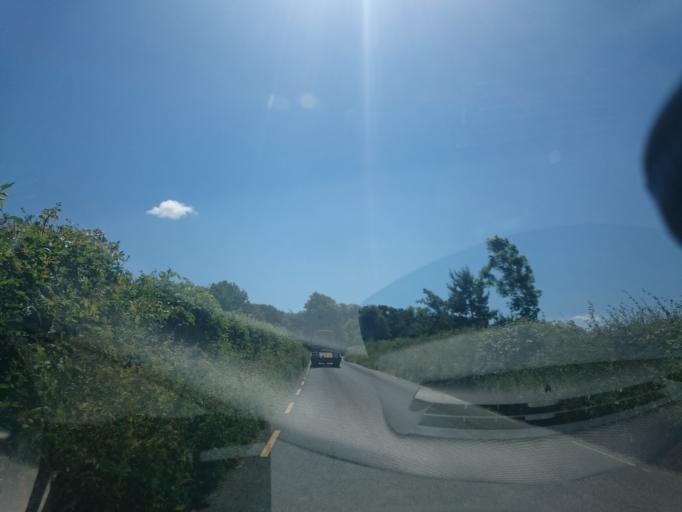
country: IE
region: Leinster
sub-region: Kilkenny
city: Graiguenamanagh
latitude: 52.6066
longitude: -6.9922
